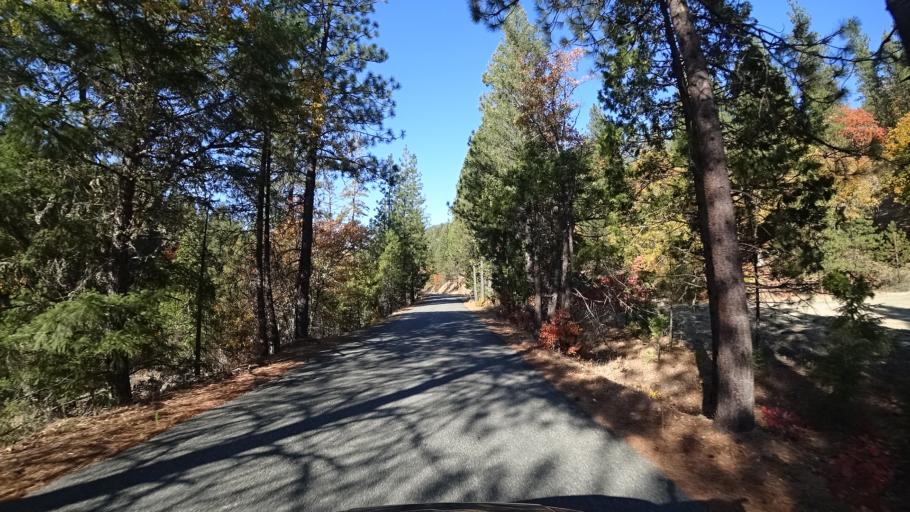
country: US
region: California
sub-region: Siskiyou County
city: Happy Camp
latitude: 41.6449
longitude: -123.0368
